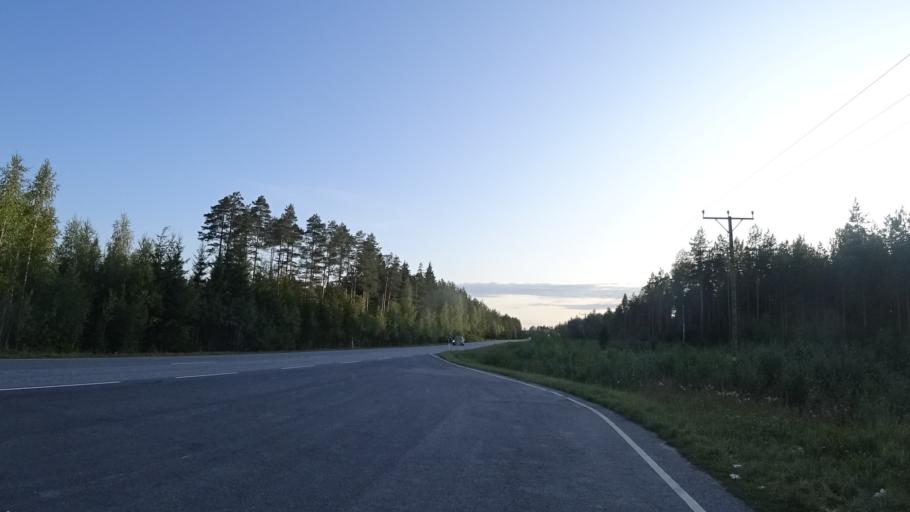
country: FI
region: South Karelia
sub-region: Lappeenranta
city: Ylaemaa
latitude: 60.8134
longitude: 28.0615
